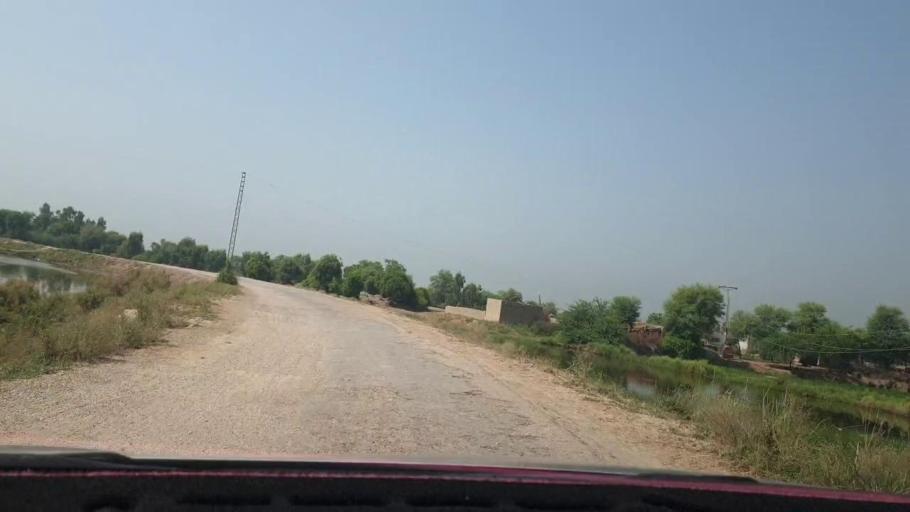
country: PK
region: Sindh
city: Warah
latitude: 27.4173
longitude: 67.8449
